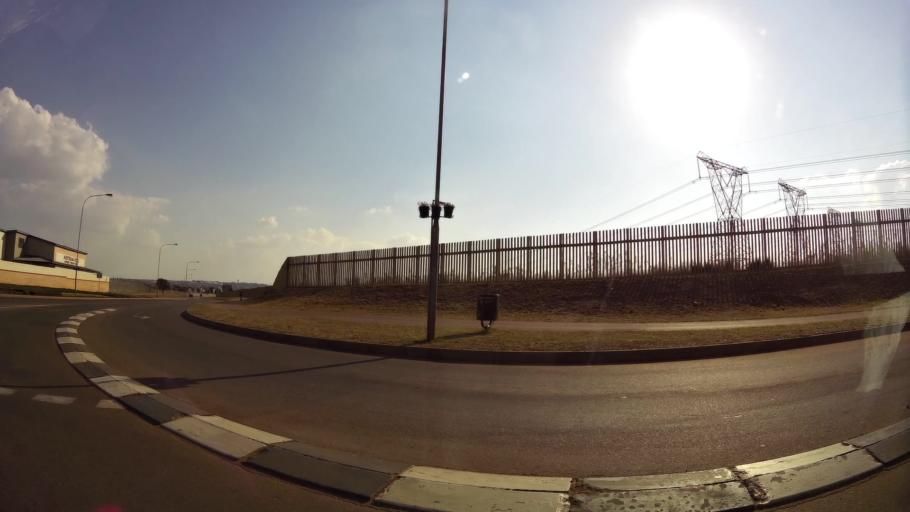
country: ZA
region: Gauteng
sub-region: City of Tshwane Metropolitan Municipality
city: Centurion
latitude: -25.9182
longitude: 28.2098
